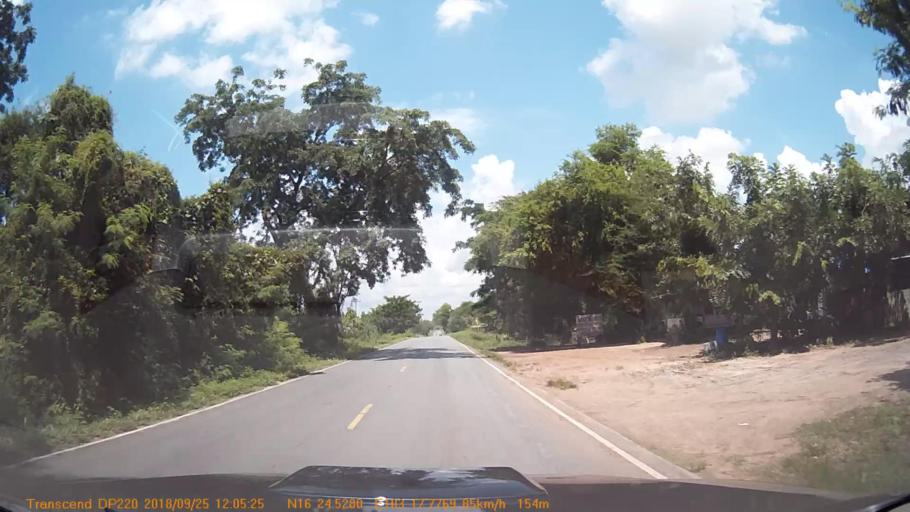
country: TH
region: Kalasin
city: Yang Talat
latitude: 16.4088
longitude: 103.2963
